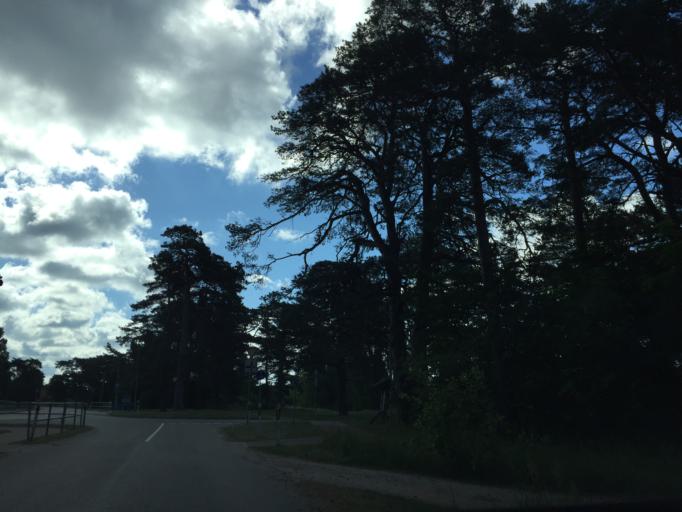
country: LV
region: Ventspils
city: Ventspils
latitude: 57.4397
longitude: 21.6136
